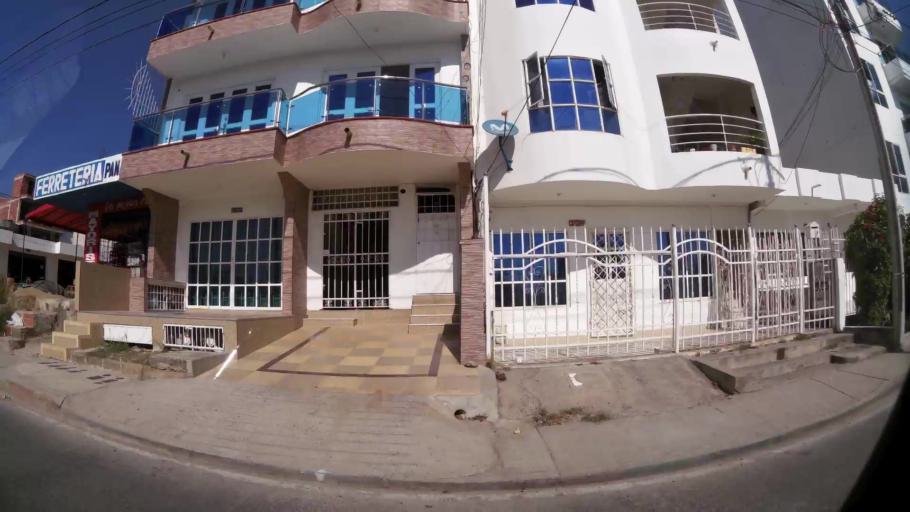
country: CO
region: Bolivar
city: Cartagena
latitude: 10.3923
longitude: -75.4720
